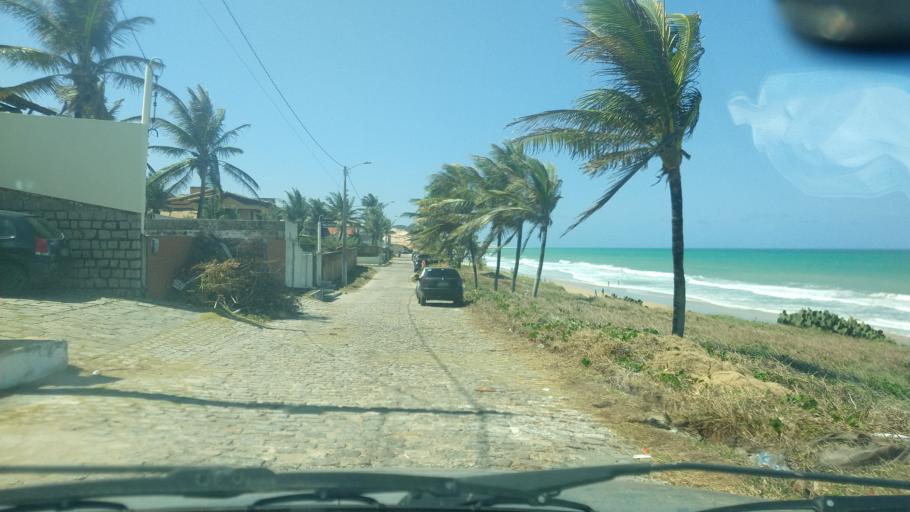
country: BR
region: Rio Grande do Norte
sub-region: Parnamirim
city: Parnamirim
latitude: -5.9492
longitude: -35.1533
